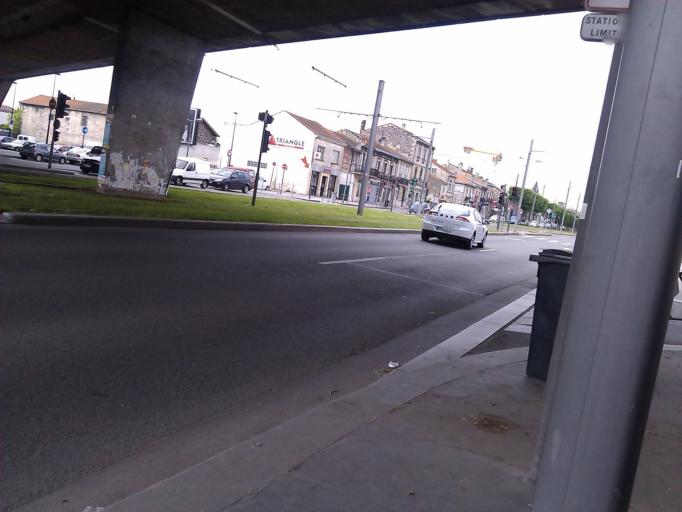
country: FR
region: Aquitaine
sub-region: Departement de la Gironde
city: Cenon
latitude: 44.8535
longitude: -0.5384
